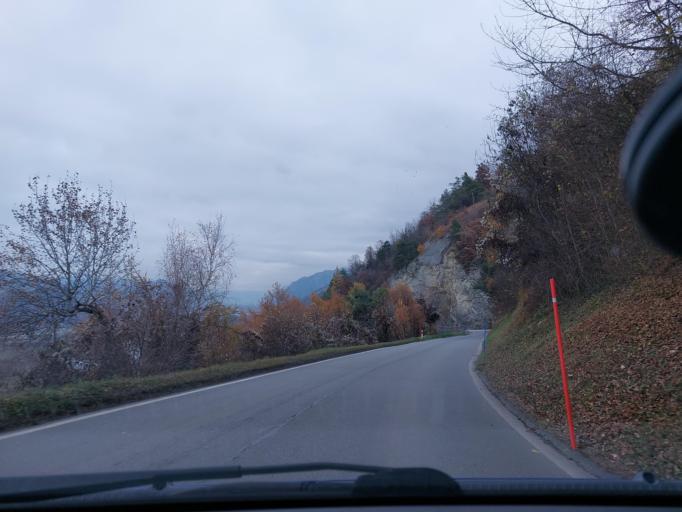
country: CH
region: Valais
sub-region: Conthey District
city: Basse-Nendaz
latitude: 46.1973
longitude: 7.2893
